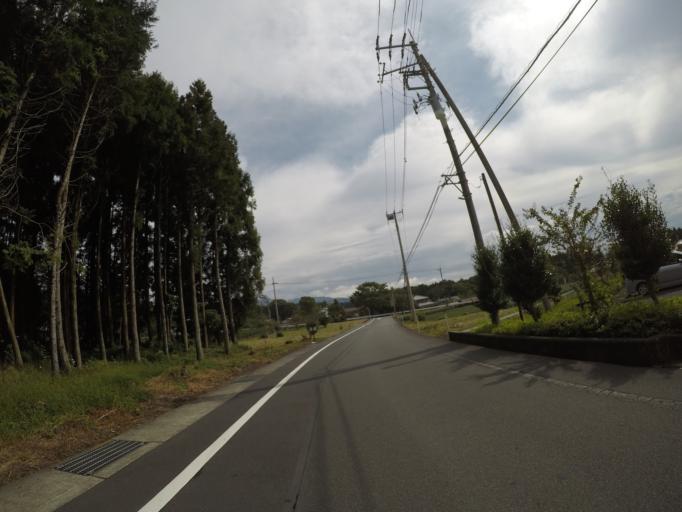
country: JP
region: Shizuoka
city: Fuji
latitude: 35.2268
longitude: 138.6889
